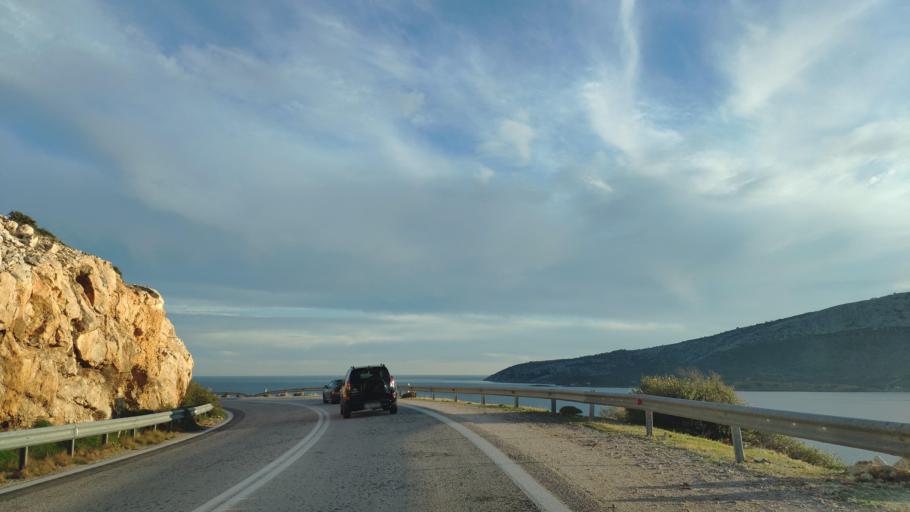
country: GR
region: Attica
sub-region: Nomarchia Anatolikis Attikis
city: Palaia Fokaia
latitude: 37.6693
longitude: 23.9522
